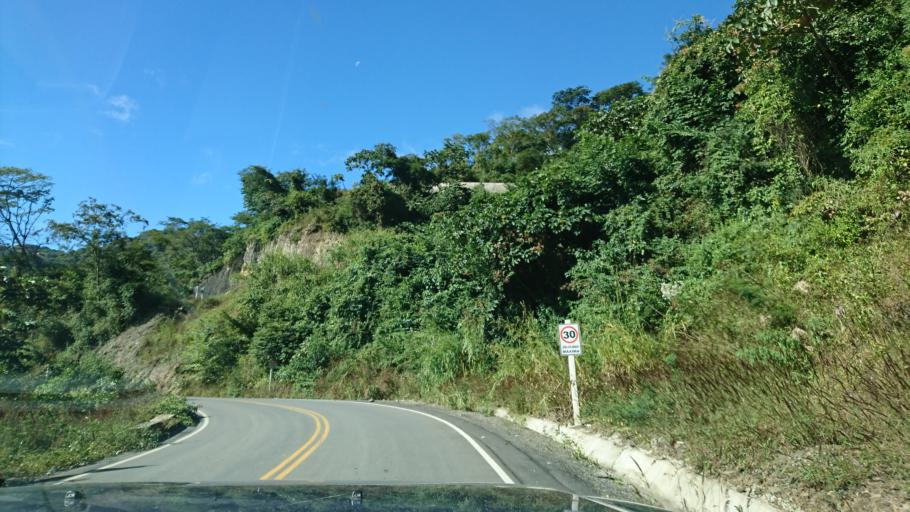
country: BO
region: La Paz
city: Coroico
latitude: -16.1998
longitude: -67.7413
